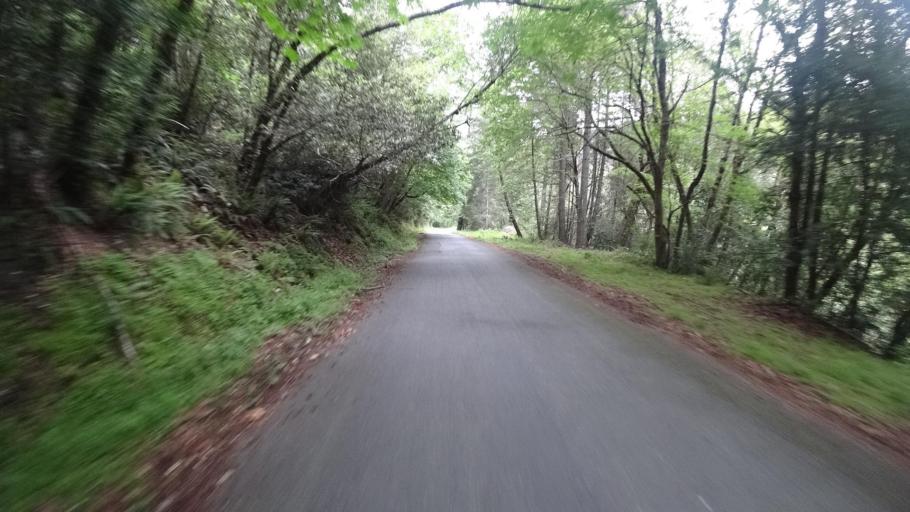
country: US
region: California
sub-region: Humboldt County
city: Willow Creek
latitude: 41.2040
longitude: -123.7561
